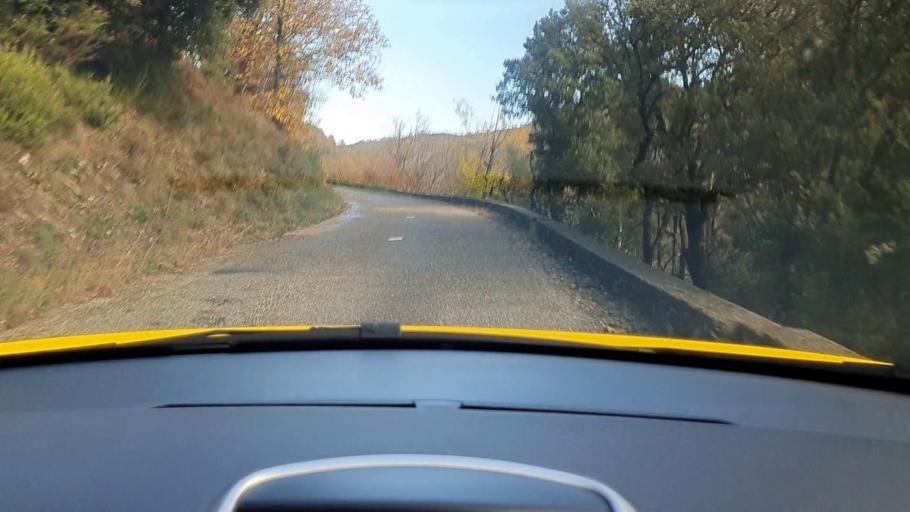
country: FR
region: Languedoc-Roussillon
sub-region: Departement du Gard
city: Valleraugue
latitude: 44.1734
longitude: 3.6554
